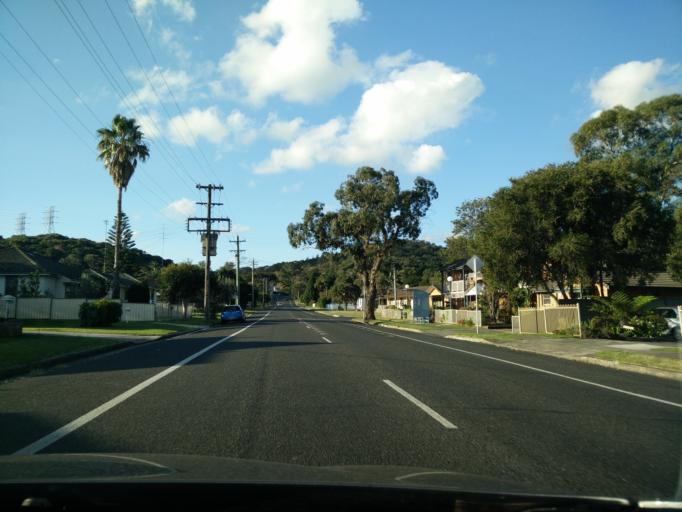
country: AU
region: New South Wales
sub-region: Wollongong
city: Berkeley
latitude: -34.4744
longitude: 150.8412
